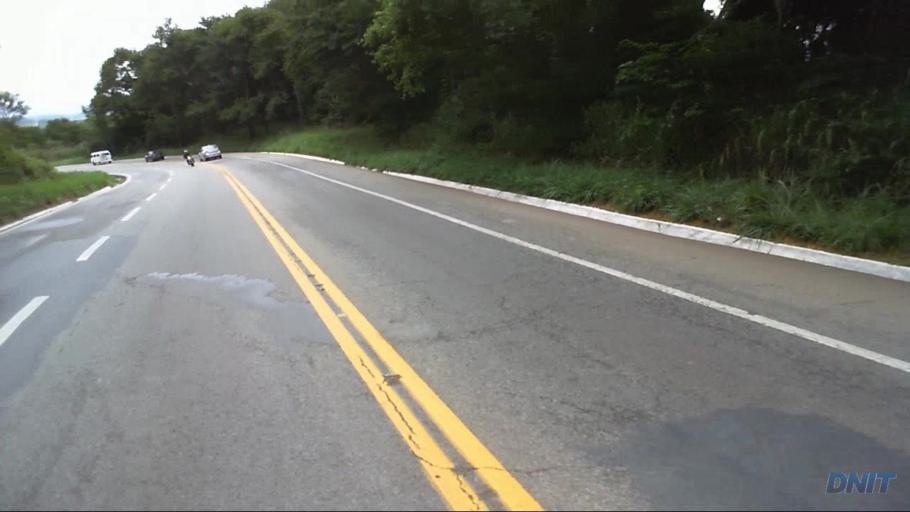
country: BR
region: Minas Gerais
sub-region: Caete
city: Caete
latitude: -19.7424
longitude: -43.5201
